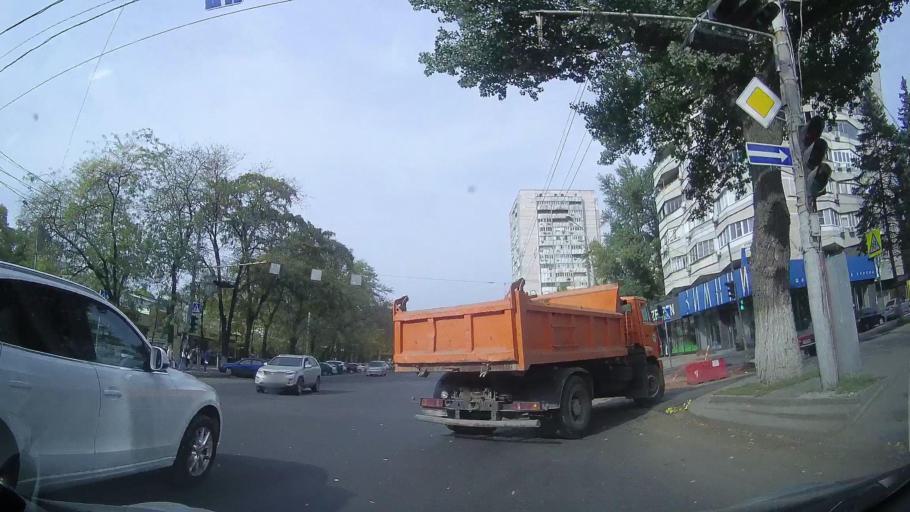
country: RU
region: Rostov
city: Rostov-na-Donu
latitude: 47.2334
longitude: 39.7132
